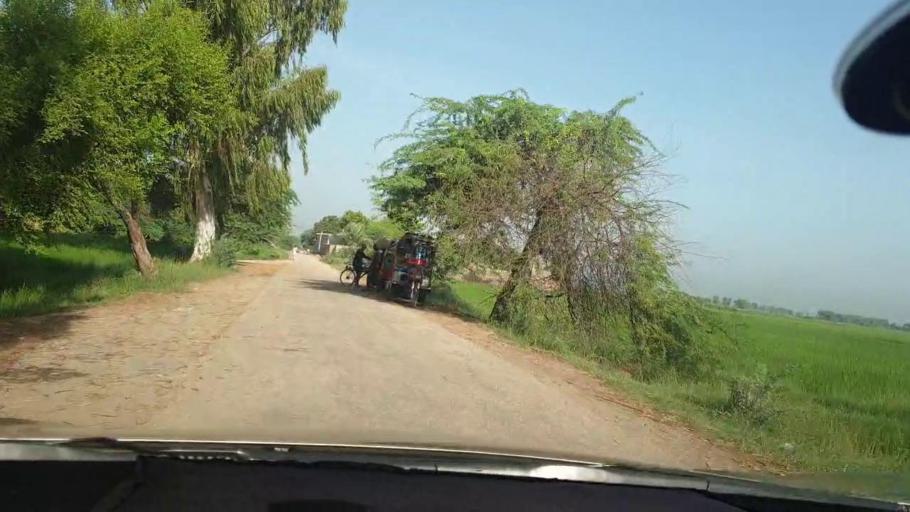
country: PK
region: Sindh
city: Kambar
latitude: 27.6533
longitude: 68.0350
